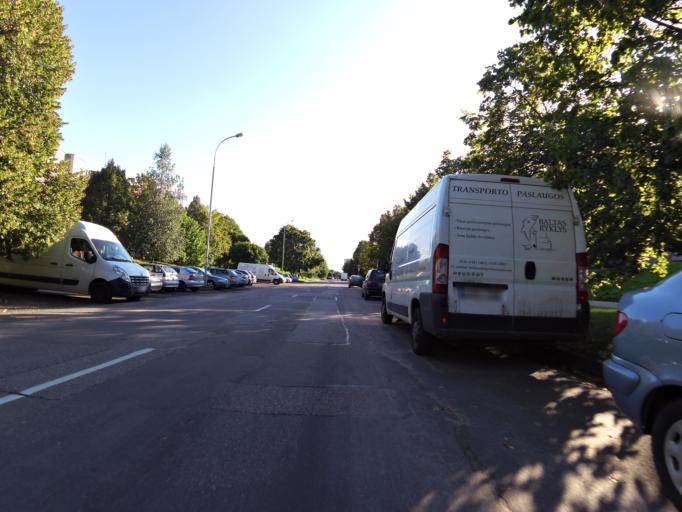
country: LT
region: Vilnius County
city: Justiniskes
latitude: 54.7108
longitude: 25.2140
